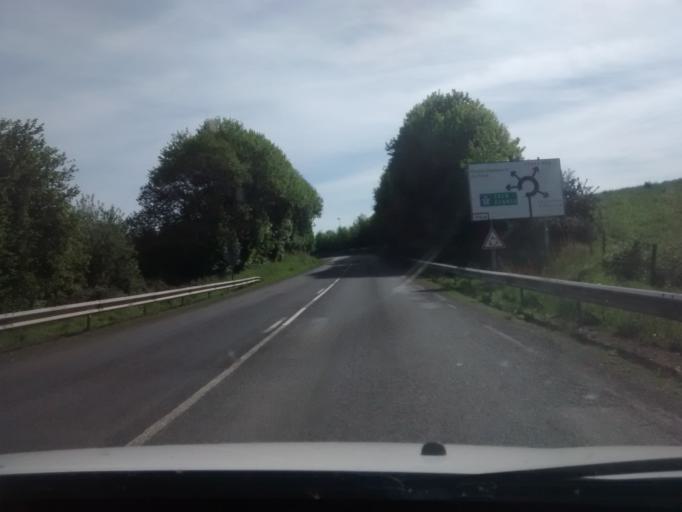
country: FR
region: Brittany
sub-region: Departement d'Ille-et-Vilaine
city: Lecousse
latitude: 48.3508
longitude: -1.2372
